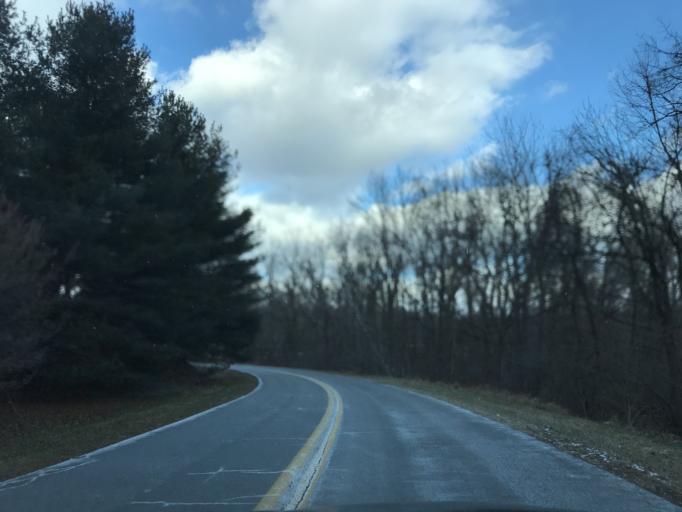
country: US
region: Maryland
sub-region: Baltimore County
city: Hunt Valley
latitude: 39.5493
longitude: -76.6641
